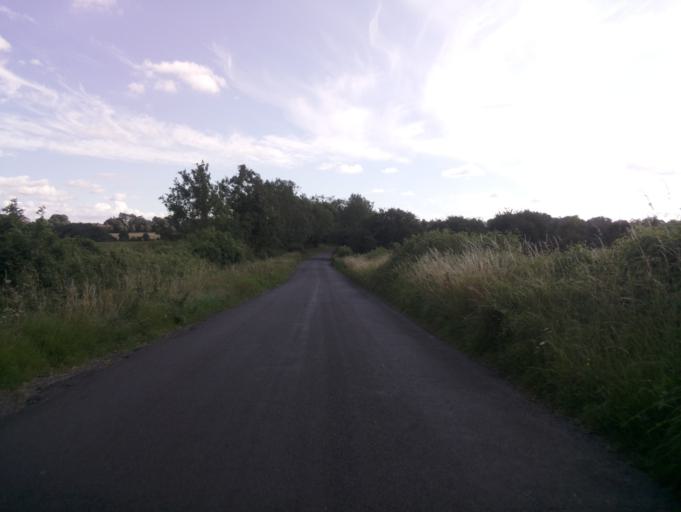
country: GB
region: England
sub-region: Gloucestershire
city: Tetbury
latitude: 51.6543
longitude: -2.1437
